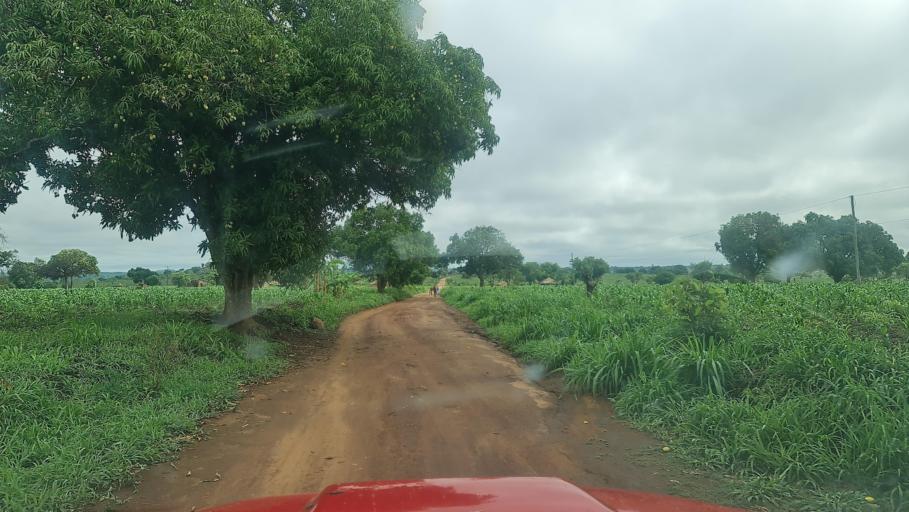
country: MW
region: Southern Region
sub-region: Nsanje District
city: Nsanje
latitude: -17.2102
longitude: 35.6789
